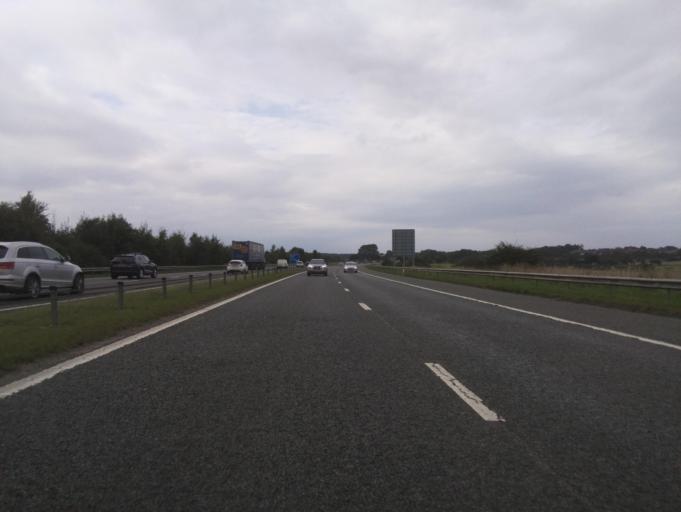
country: GB
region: England
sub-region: County Durham
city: West Cornforth
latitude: 54.7166
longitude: -1.5190
